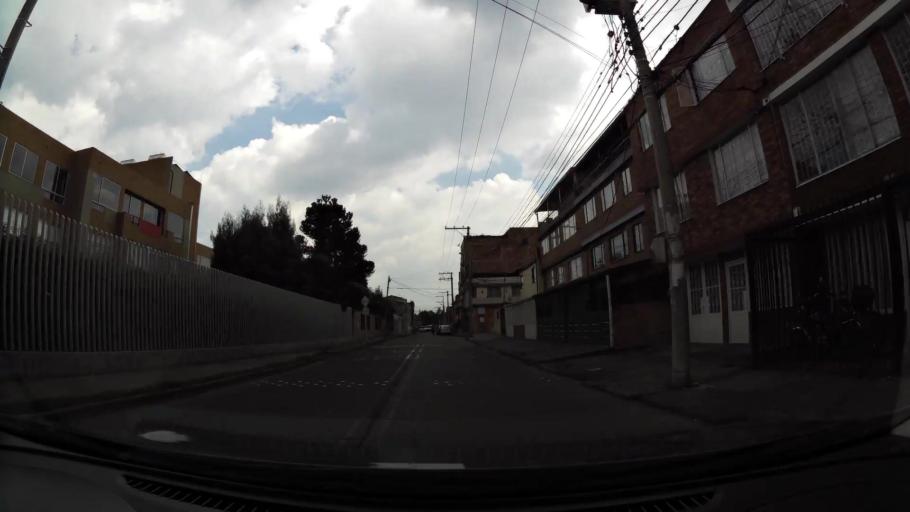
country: CO
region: Cundinamarca
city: La Calera
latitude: 4.7415
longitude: -74.0385
